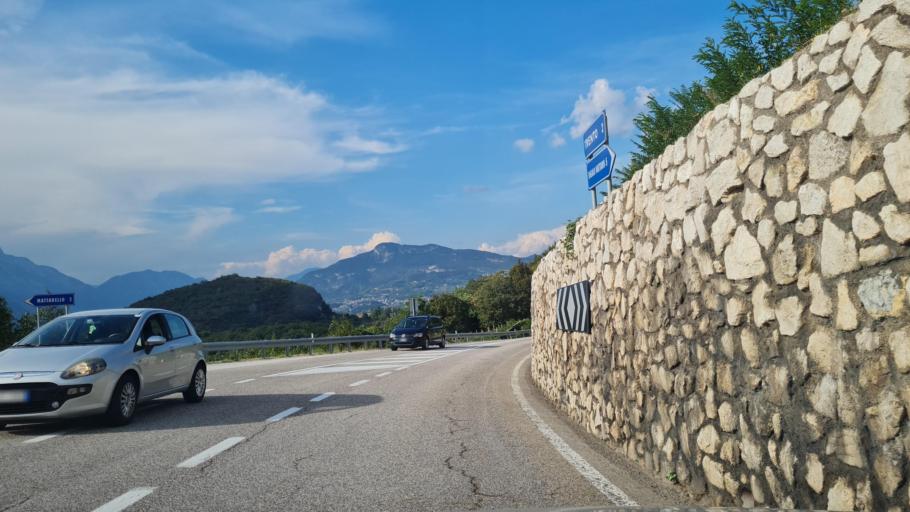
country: IT
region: Trentino-Alto Adige
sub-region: Provincia di Trento
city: Mattarello
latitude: 46.0220
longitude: 11.1449
